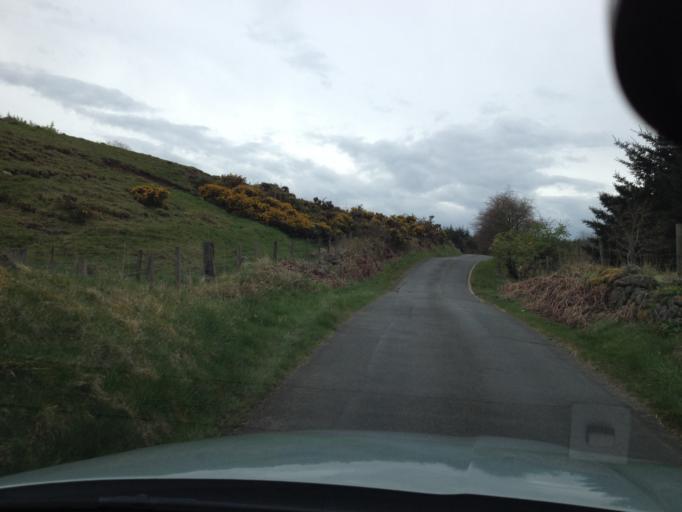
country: GB
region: Scotland
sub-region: West Lothian
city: Linlithgow
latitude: 55.9382
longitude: -3.6044
